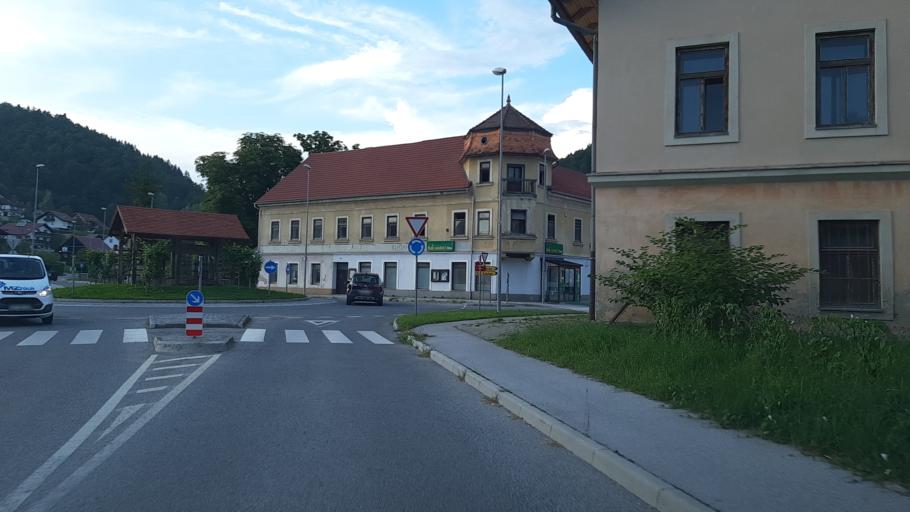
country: SI
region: Sentjur pri Celju
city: Sentjur
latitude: 46.1867
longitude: 15.4311
